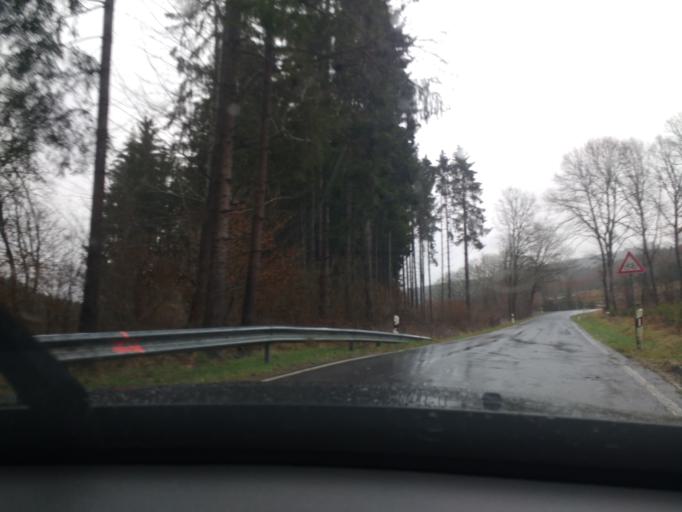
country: DE
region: Rheinland-Pfalz
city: Schomerich
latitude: 49.6389
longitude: 6.7190
